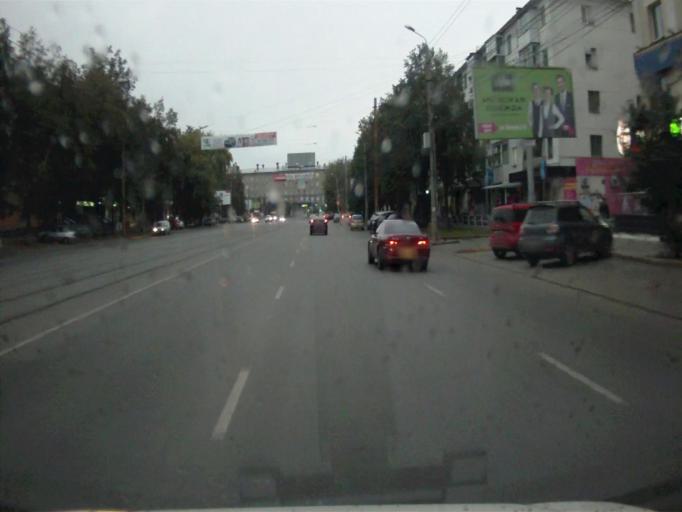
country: RU
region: Chelyabinsk
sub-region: Gorod Chelyabinsk
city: Chelyabinsk
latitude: 55.1808
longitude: 61.3994
